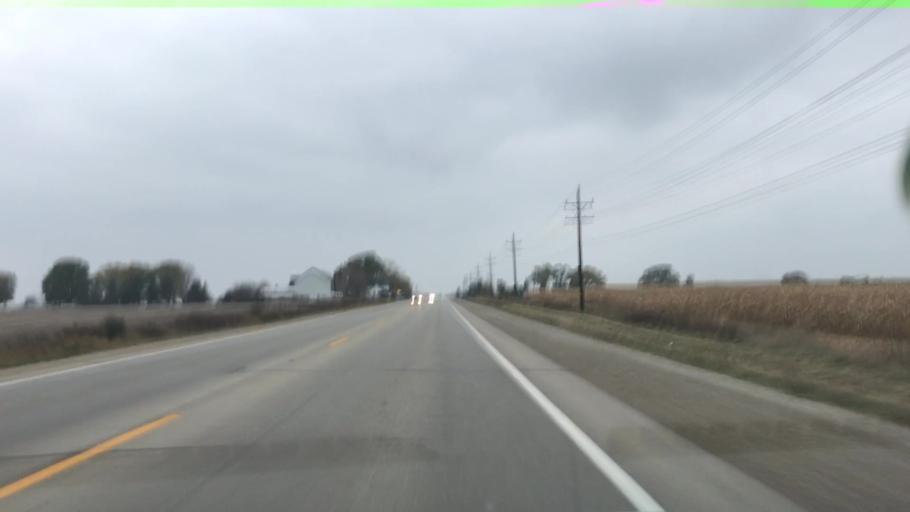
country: US
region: Wisconsin
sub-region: Outagamie County
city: Seymour
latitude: 44.5003
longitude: -88.3034
